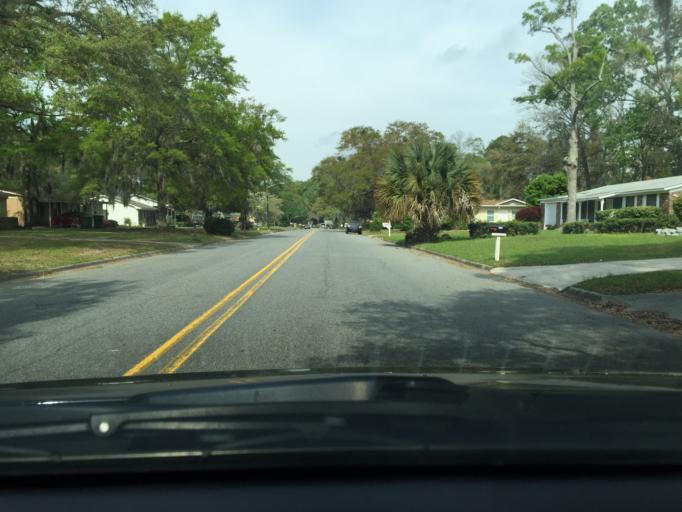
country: US
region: Georgia
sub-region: Chatham County
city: Montgomery
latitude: 31.9863
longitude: -81.1425
